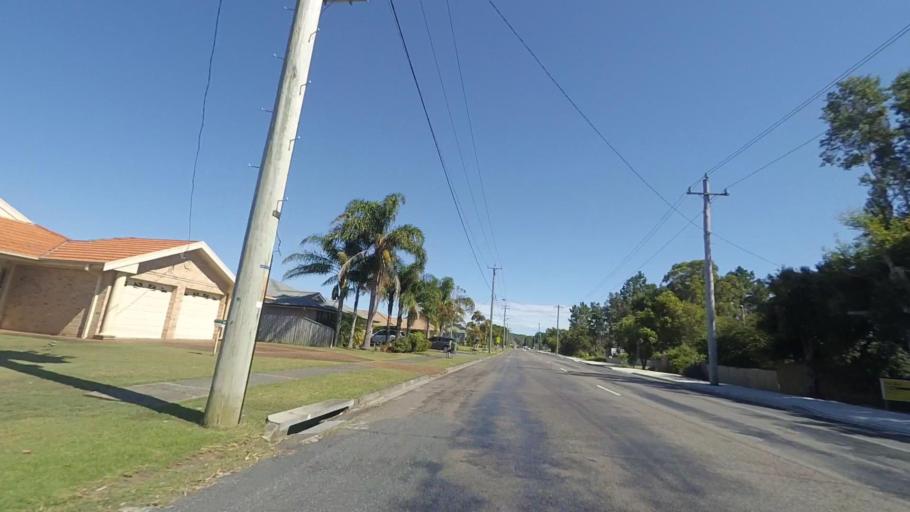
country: AU
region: New South Wales
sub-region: Great Lakes
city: Hawks Nest
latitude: -32.6549
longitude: 152.1501
